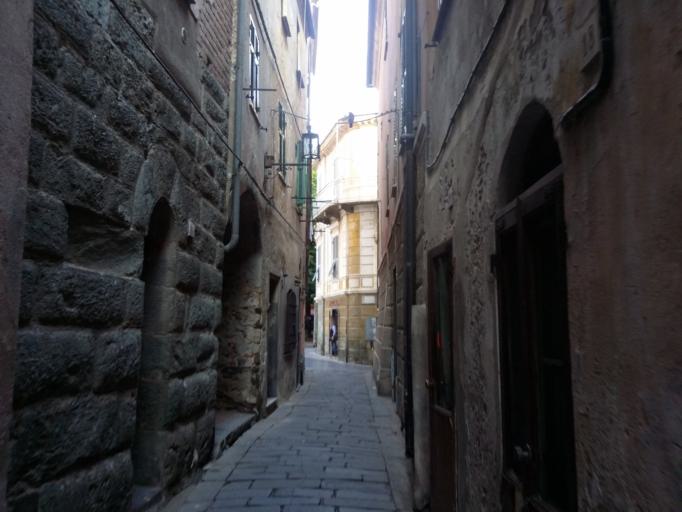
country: IT
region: Liguria
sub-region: Provincia di Savona
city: Noli
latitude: 44.2054
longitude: 8.4151
